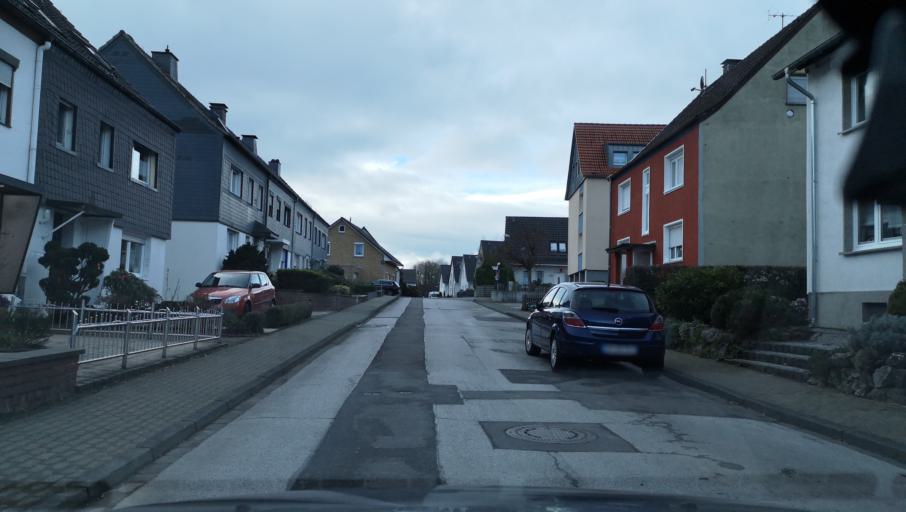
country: DE
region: North Rhine-Westphalia
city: Radevormwald
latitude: 51.1983
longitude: 7.3663
